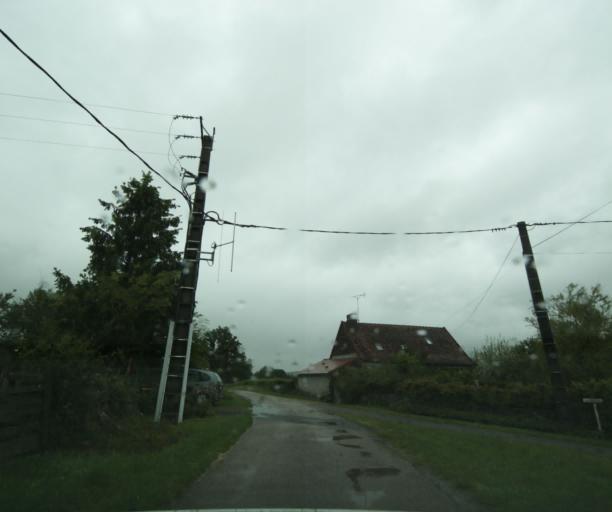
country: FR
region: Bourgogne
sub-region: Departement de Saone-et-Loire
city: Saint-Vallier
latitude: 46.5373
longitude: 4.3943
